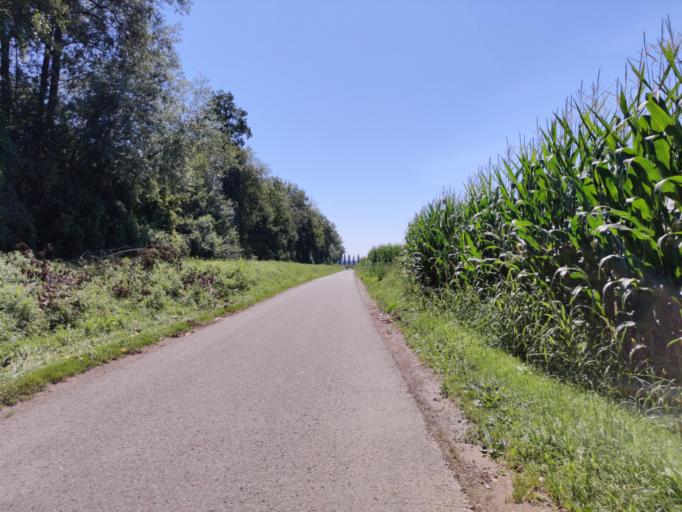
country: AT
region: Styria
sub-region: Politischer Bezirk Leibnitz
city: Ragnitz
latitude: 46.8314
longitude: 15.5590
